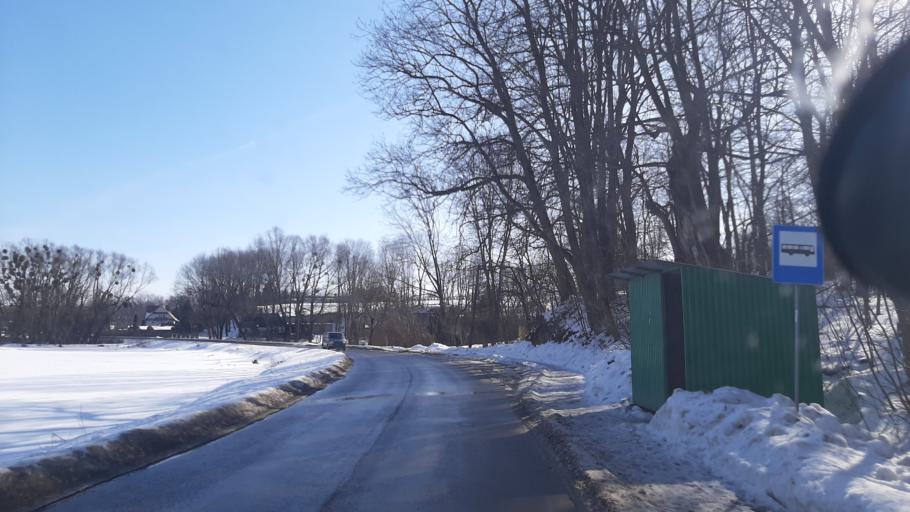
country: PL
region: Lublin Voivodeship
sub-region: Powiat pulawski
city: Wawolnica
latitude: 51.3566
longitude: 22.1233
